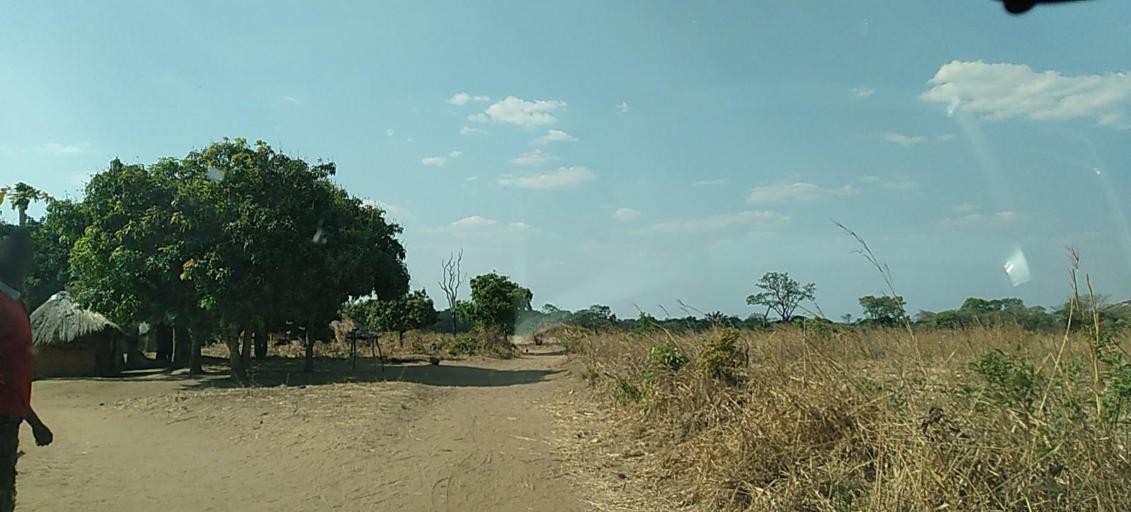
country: ZM
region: North-Western
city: Kalengwa
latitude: -13.0590
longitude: 24.9552
